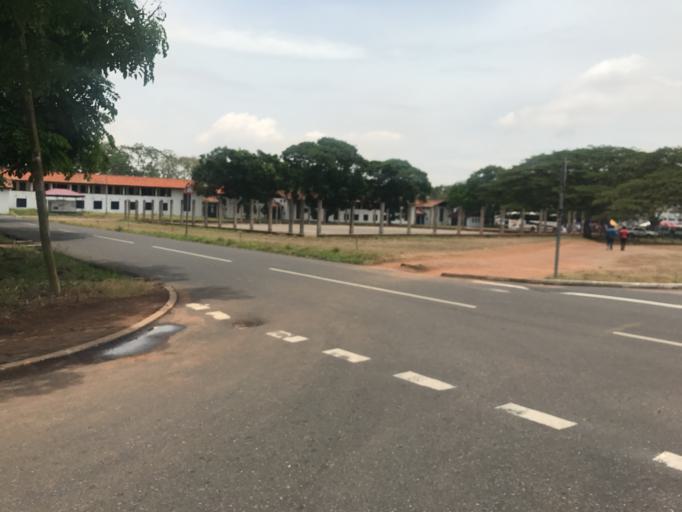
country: GH
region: Greater Accra
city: Medina Estates
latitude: 5.6497
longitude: -0.1870
